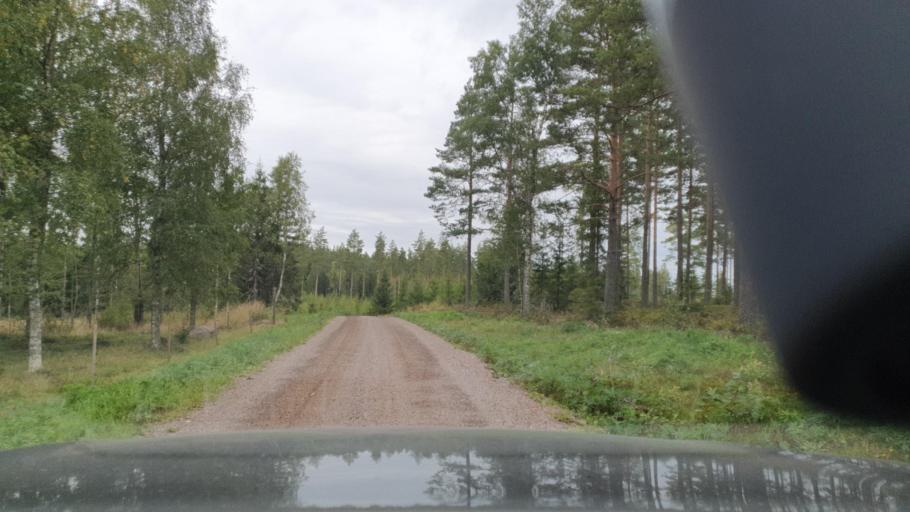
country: SE
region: Vaermland
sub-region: Torsby Kommun
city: Torsby
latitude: 59.9462
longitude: 12.7952
